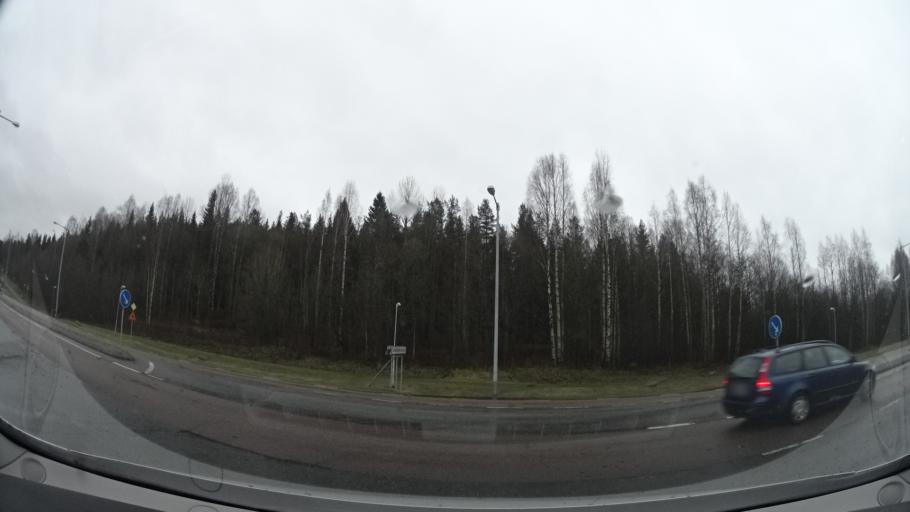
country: SE
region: Vaesterbotten
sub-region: Skelleftea Kommun
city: Skelleftea
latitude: 64.7606
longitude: 20.9325
